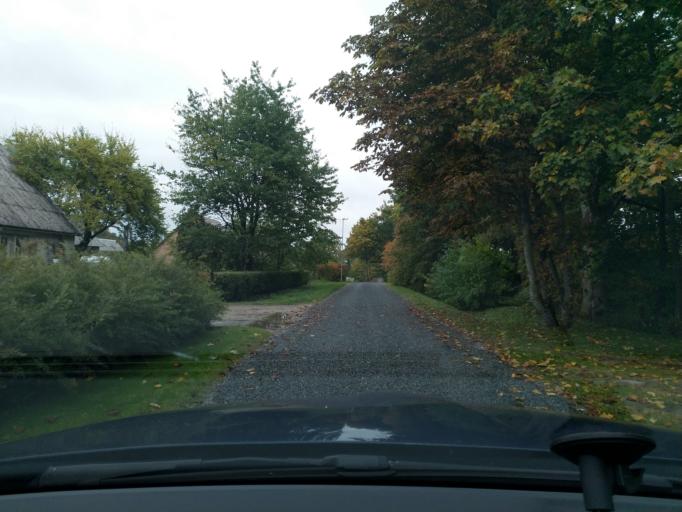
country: LV
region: Alsunga
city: Alsunga
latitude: 57.0208
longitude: 21.6870
